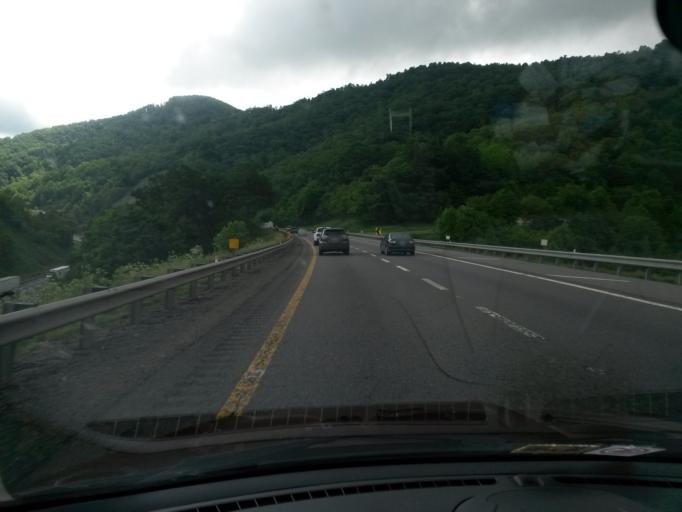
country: US
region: Virginia
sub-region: Carroll County
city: Cana
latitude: 36.6201
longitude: -80.7386
